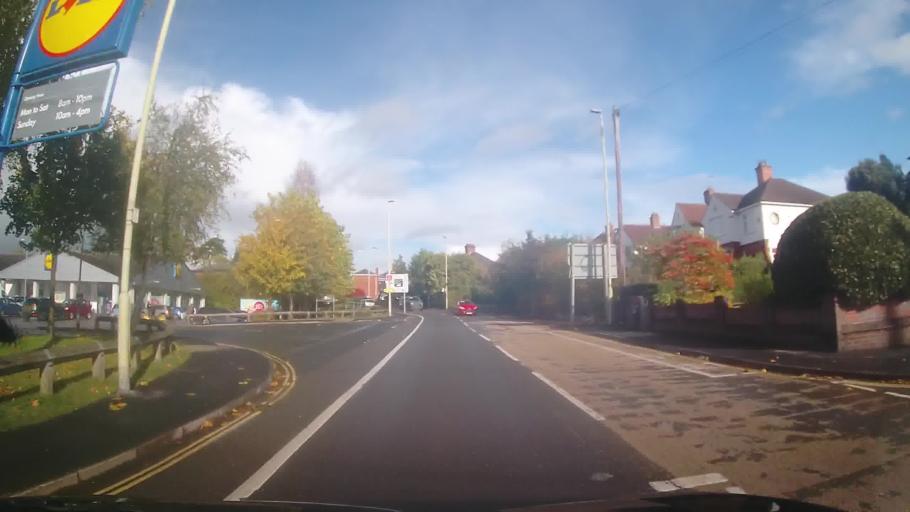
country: GB
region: England
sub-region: Shropshire
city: Whitchurch
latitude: 52.9673
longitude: -2.6793
